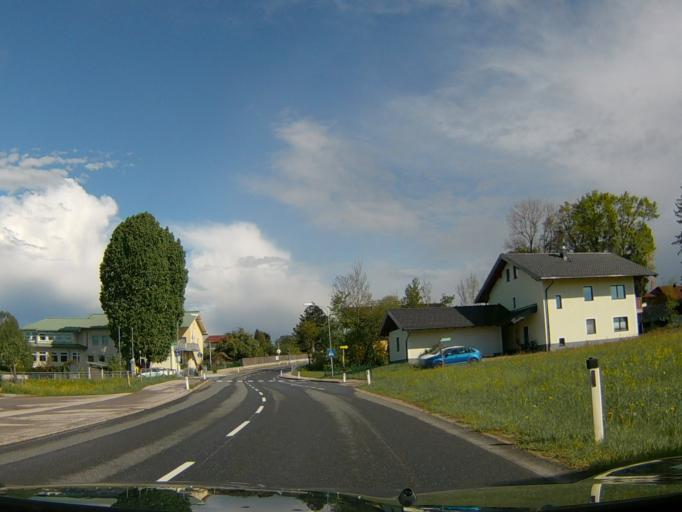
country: AT
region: Salzburg
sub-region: Politischer Bezirk Salzburg-Umgebung
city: Plainfeld
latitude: 47.8592
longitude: 13.1720
